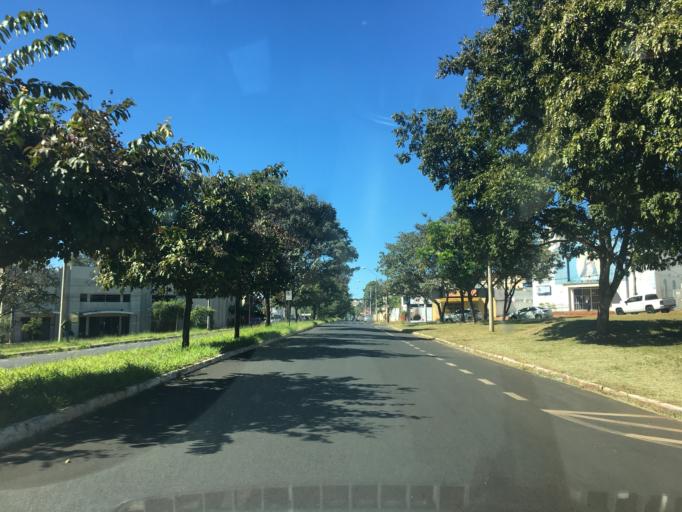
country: BR
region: Minas Gerais
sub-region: Uberlandia
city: Uberlandia
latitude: -18.9332
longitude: -48.2857
